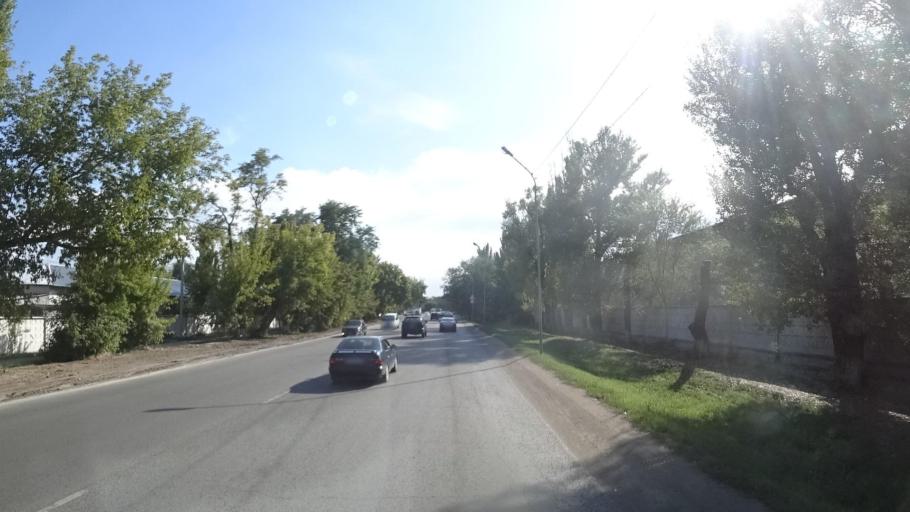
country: KZ
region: Almaty Oblysy
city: Energeticheskiy
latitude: 43.3830
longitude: 76.9987
